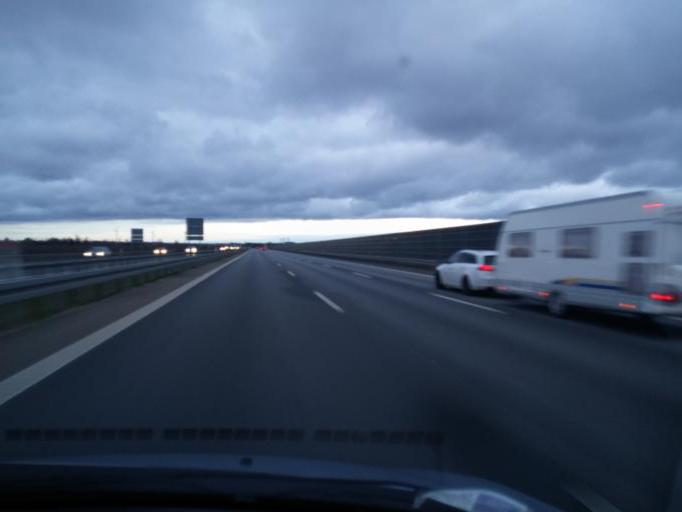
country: DK
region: South Denmark
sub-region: Middelfart Kommune
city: Norre Aby
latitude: 55.4826
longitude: 9.8654
